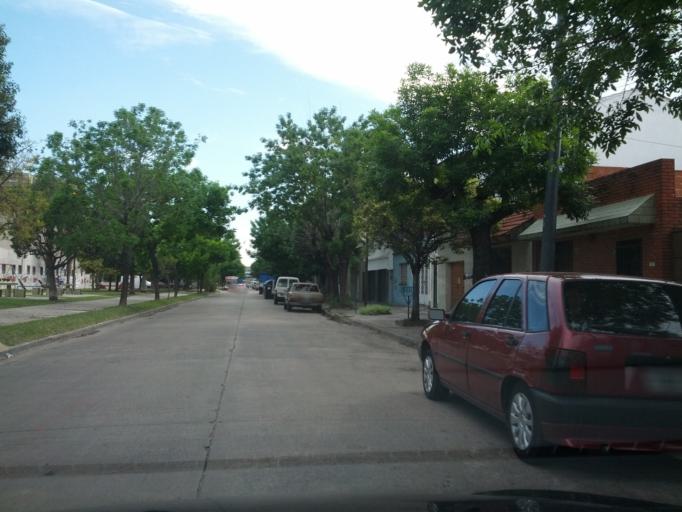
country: AR
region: Buenos Aires F.D.
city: Villa Lugano
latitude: -34.6506
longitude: -58.4272
